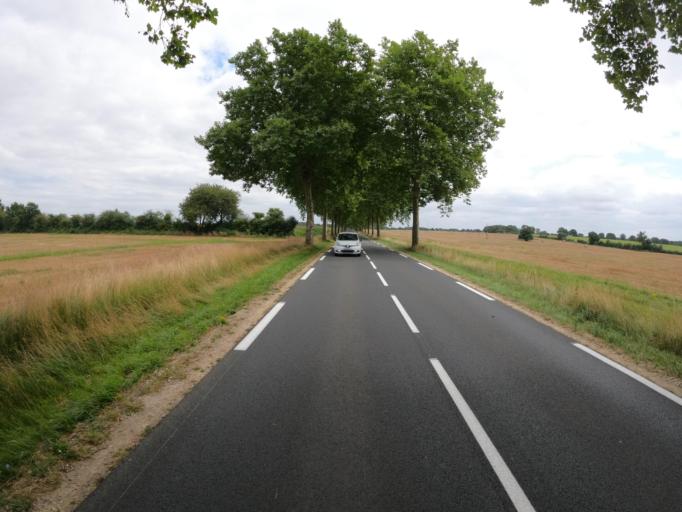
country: FR
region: Poitou-Charentes
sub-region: Departement de la Vienne
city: Charroux
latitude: 46.1376
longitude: 0.4408
